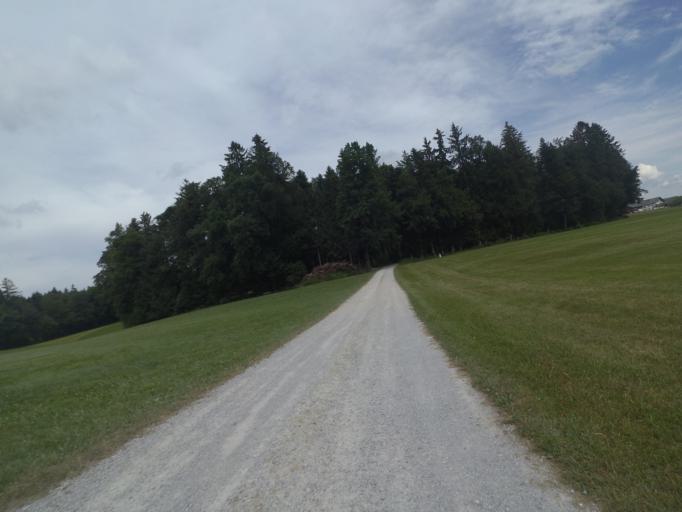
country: AT
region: Salzburg
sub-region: Politischer Bezirk Salzburg-Umgebung
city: Elixhausen
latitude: 47.8823
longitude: 13.0849
